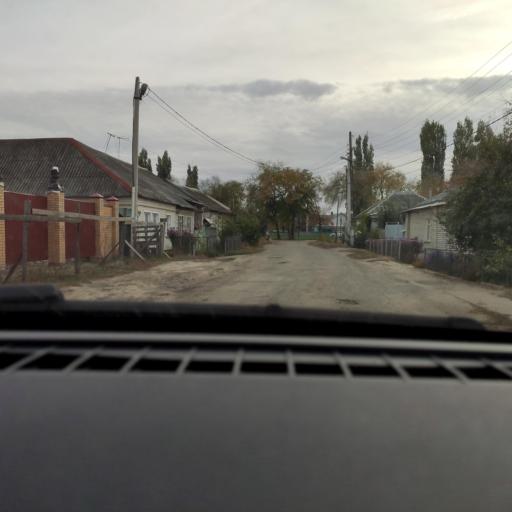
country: RU
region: Voronezj
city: Voronezh
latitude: 51.6683
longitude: 39.2649
